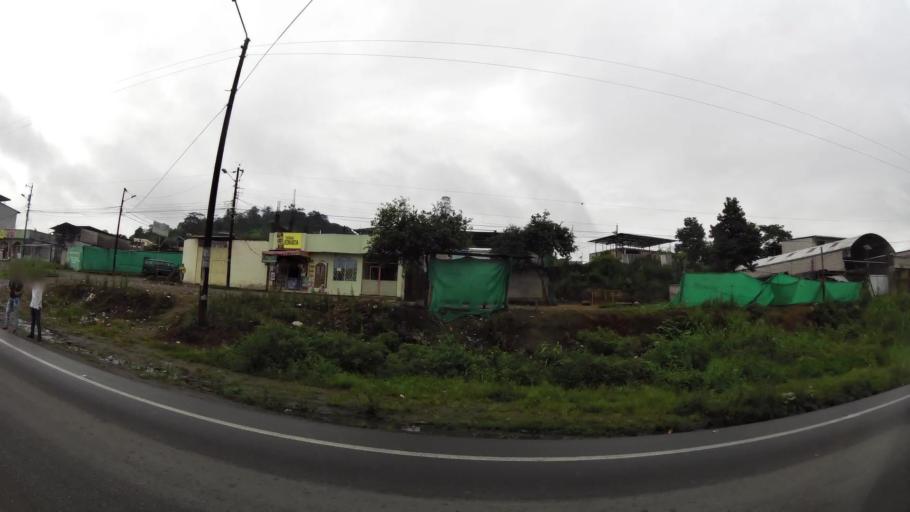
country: EC
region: Santo Domingo de los Tsachilas
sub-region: Canton Santo Domingo de los Colorados
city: Santo Domingo de los Colorados
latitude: -0.2448
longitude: -79.1981
